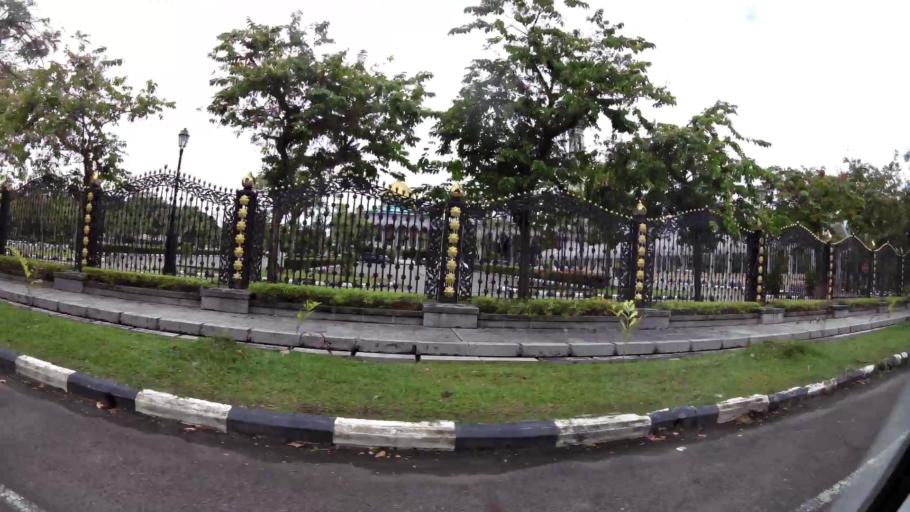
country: BN
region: Brunei and Muara
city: Bandar Seri Begawan
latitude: 4.8991
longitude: 114.9228
